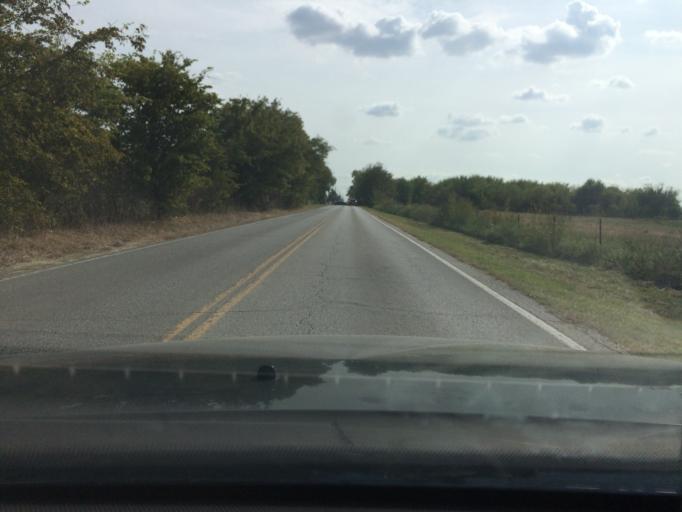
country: US
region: Oklahoma
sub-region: Tulsa County
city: Broken Arrow
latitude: 36.1064
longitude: -95.7617
